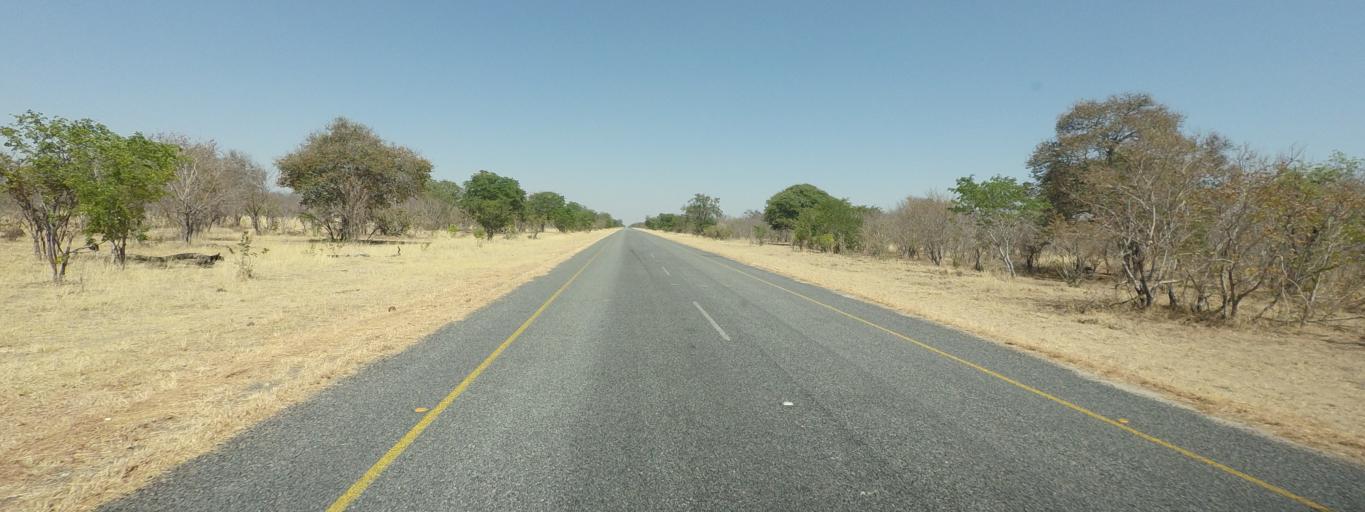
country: BW
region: North West
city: Kasane
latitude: -17.9222
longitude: 24.9230
